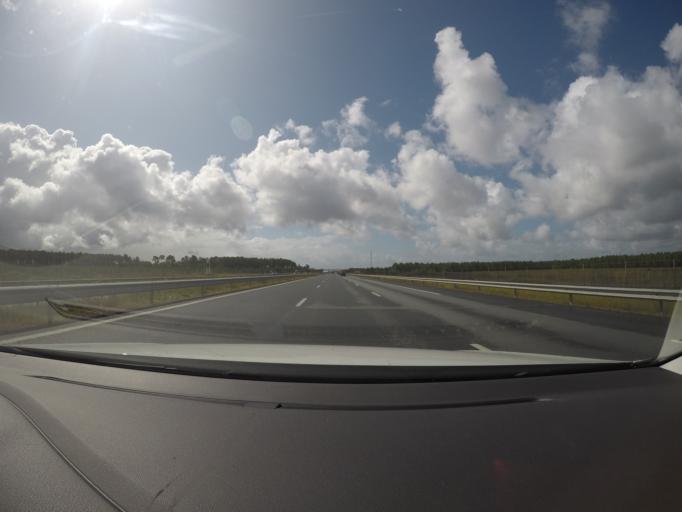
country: FR
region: Aquitaine
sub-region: Departement des Landes
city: Onesse-Laharie
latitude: 43.9964
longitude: -1.0361
